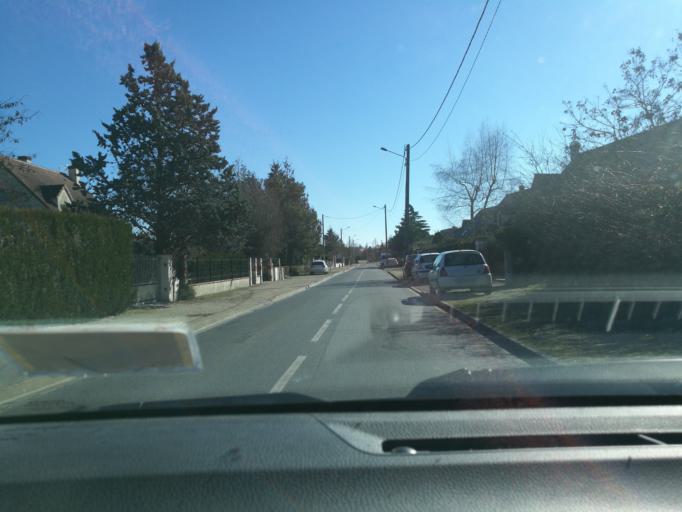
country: FR
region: Centre
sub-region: Departement du Loiret
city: Saint-Jean-le-Blanc
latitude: 47.8752
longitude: 1.9250
